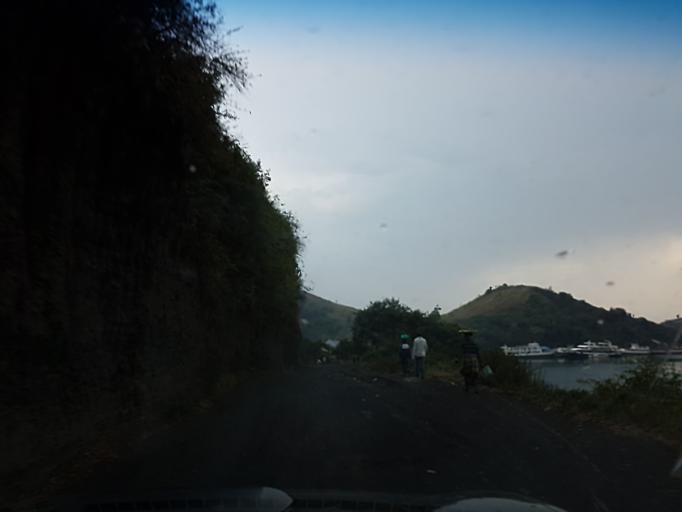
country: CD
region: Nord Kivu
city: Goma
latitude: -1.6811
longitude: 29.2221
